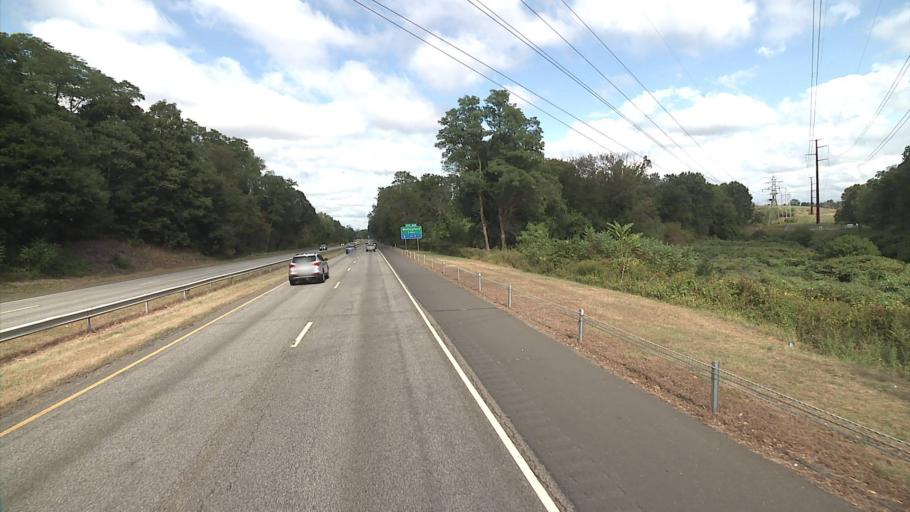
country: US
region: Connecticut
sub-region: New Haven County
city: Wallingford
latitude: 41.4402
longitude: -72.8474
